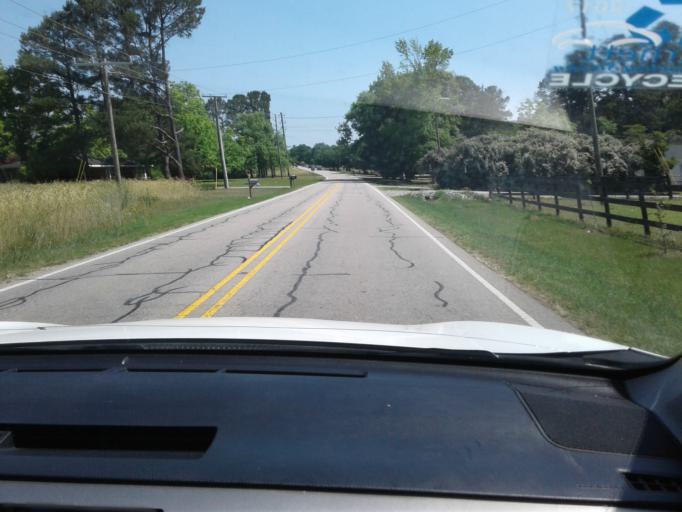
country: US
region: North Carolina
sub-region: Wake County
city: Fuquay-Varina
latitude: 35.5784
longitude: -78.8438
